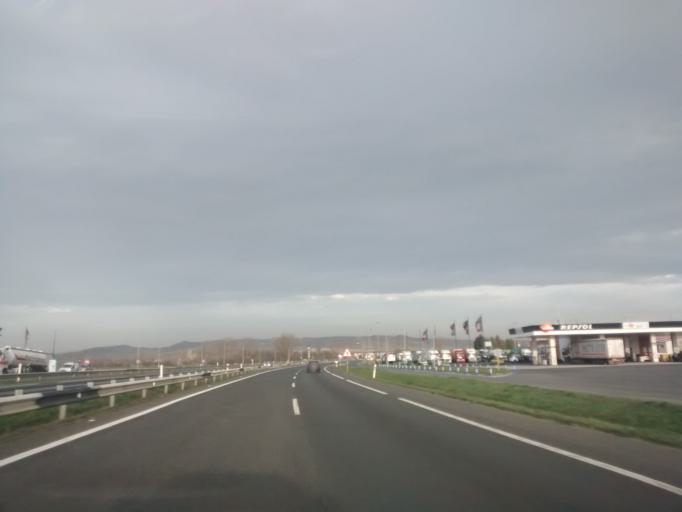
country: ES
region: Basque Country
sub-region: Provincia de Alava
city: Gasteiz / Vitoria
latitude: 42.8768
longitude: -2.7145
